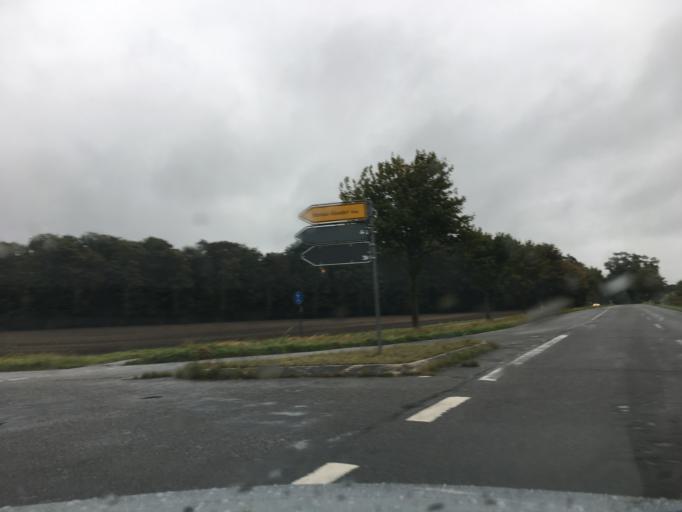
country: DE
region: Schleswig-Holstein
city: Felm
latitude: 54.3854
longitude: 10.0572
